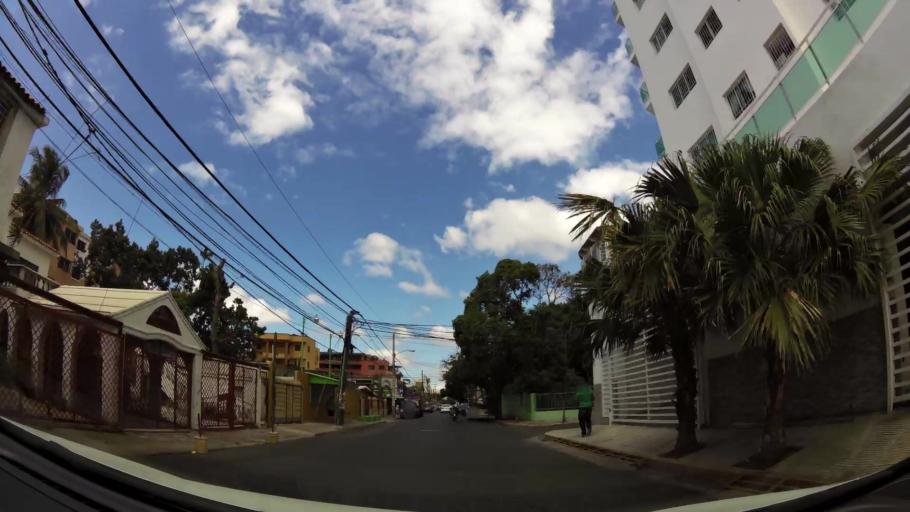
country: DO
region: Nacional
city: Bella Vista
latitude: 18.4637
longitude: -69.9464
